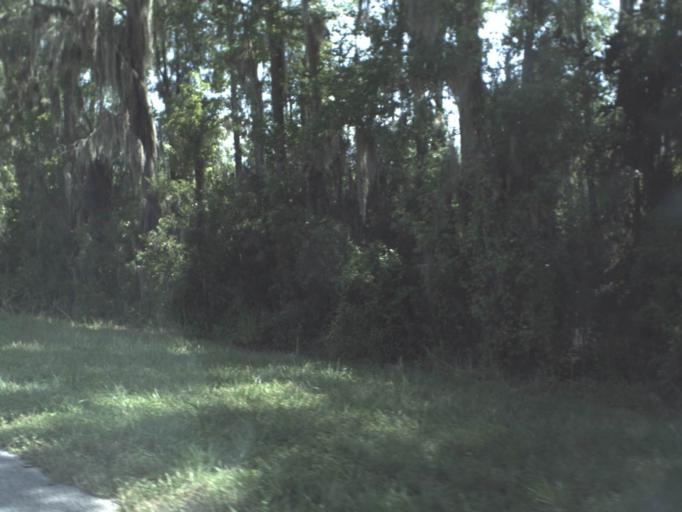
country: US
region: Florida
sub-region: Hamilton County
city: Jasper
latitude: 30.4337
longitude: -82.9337
